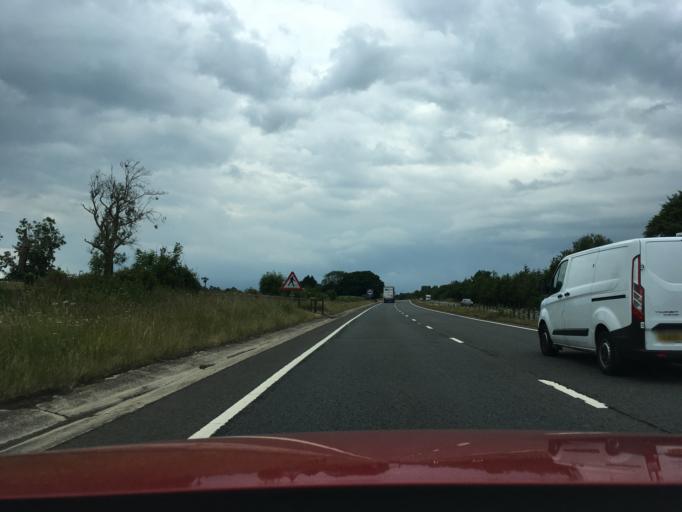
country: GB
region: England
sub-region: Gloucestershire
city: Coates
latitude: 51.7915
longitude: -2.0463
